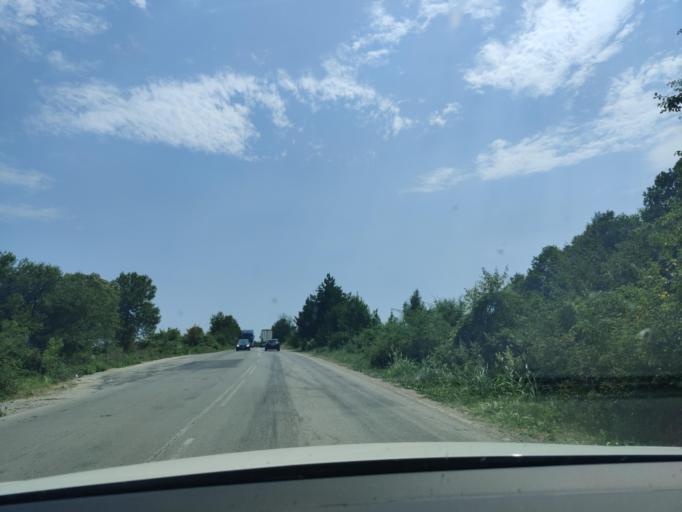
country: BG
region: Vidin
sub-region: Obshtina Ruzhintsi
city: Ruzhintsi
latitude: 43.5336
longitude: 22.9502
